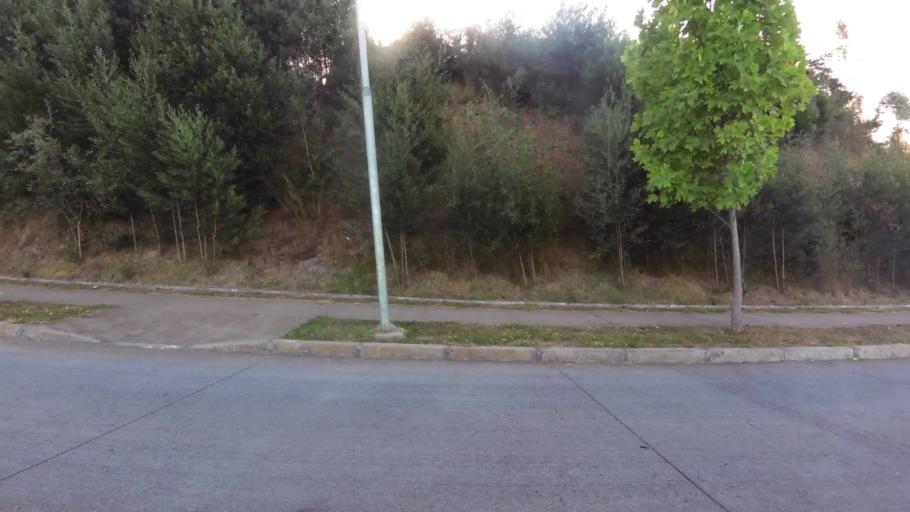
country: CL
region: Biobio
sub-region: Provincia de Concepcion
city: Concepcion
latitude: -36.8595
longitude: -73.0899
